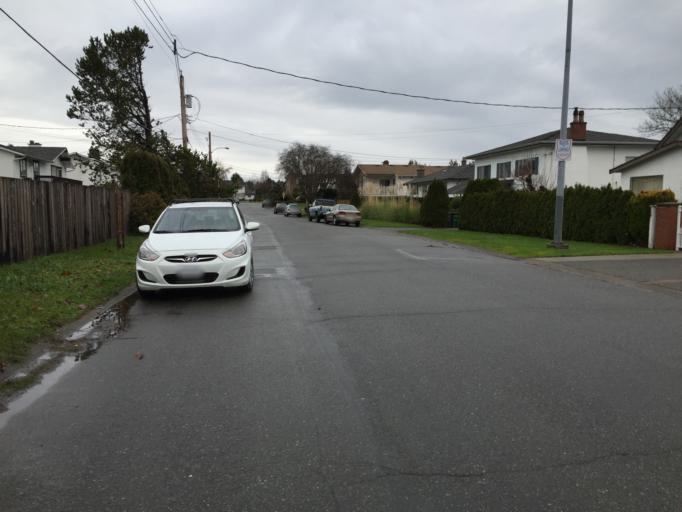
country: CA
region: British Columbia
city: Oak Bay
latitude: 48.4695
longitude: -123.3244
